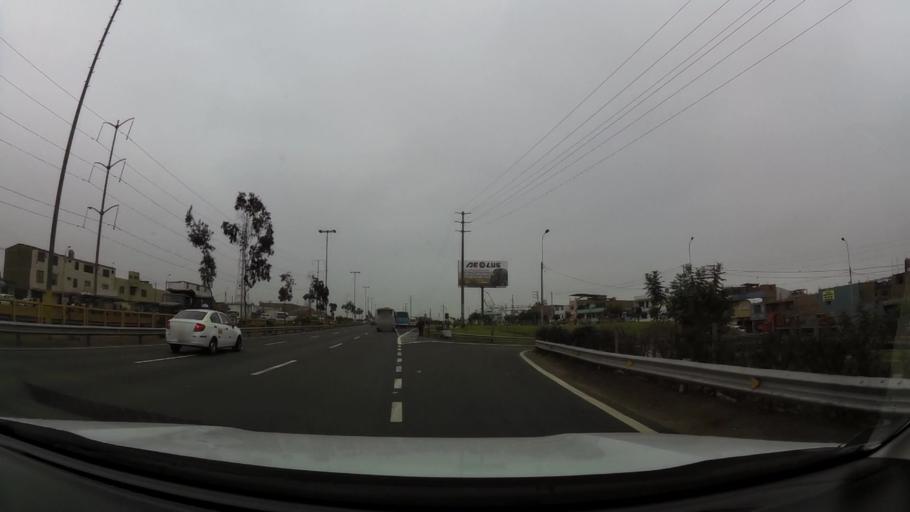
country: PE
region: Lima
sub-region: Lima
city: Surco
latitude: -12.1707
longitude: -76.9794
